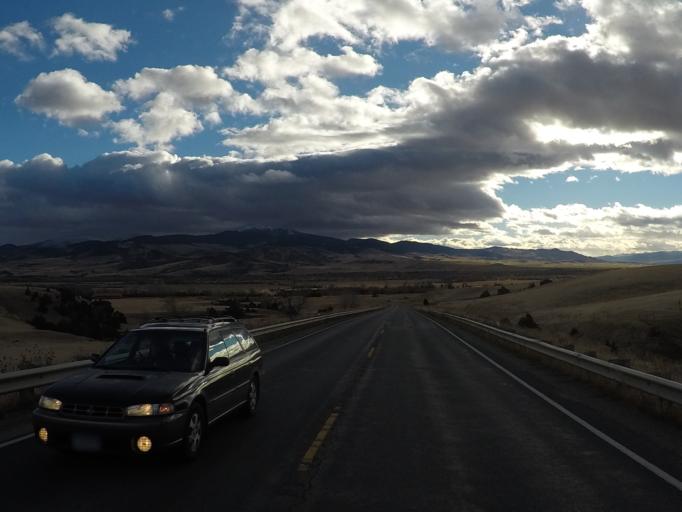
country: US
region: Montana
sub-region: Jefferson County
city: Whitehall
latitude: 45.8805
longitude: -111.9740
